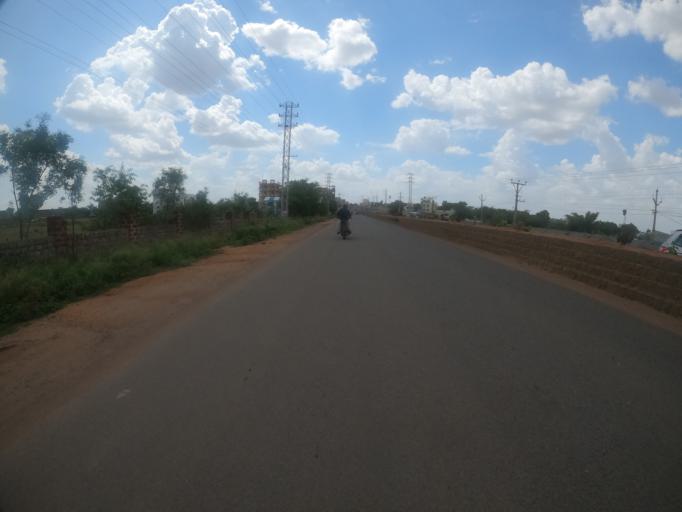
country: IN
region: Telangana
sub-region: Rangareddi
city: Sriramnagar
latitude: 17.3069
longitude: 78.1443
